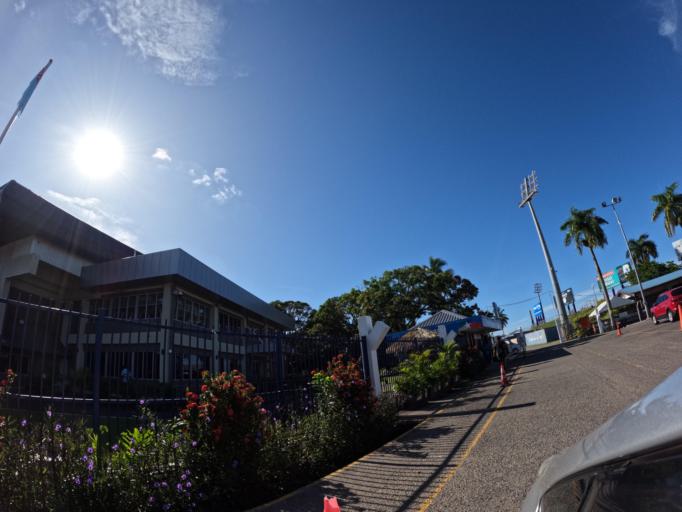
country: FJ
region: Central
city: Suva
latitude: -18.1488
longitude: 178.4501
